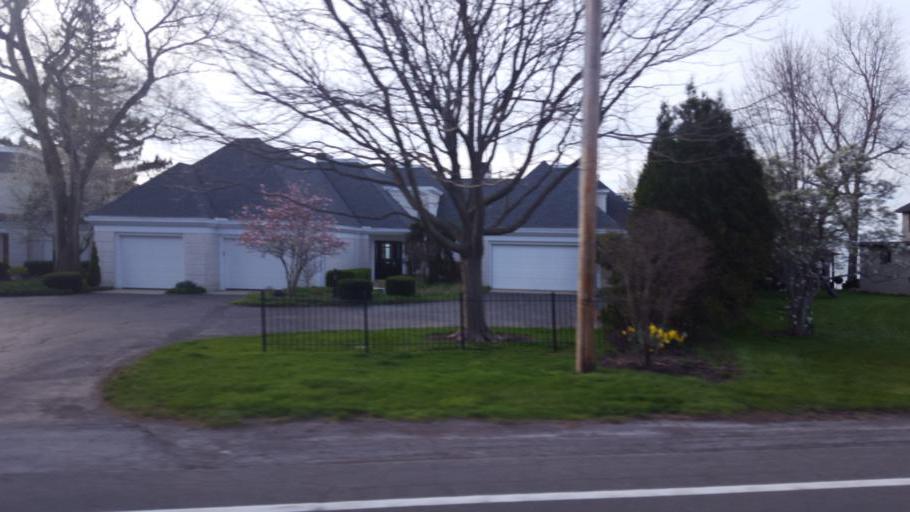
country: US
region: Ohio
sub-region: Lorain County
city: Vermilion
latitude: 41.4004
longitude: -82.4227
